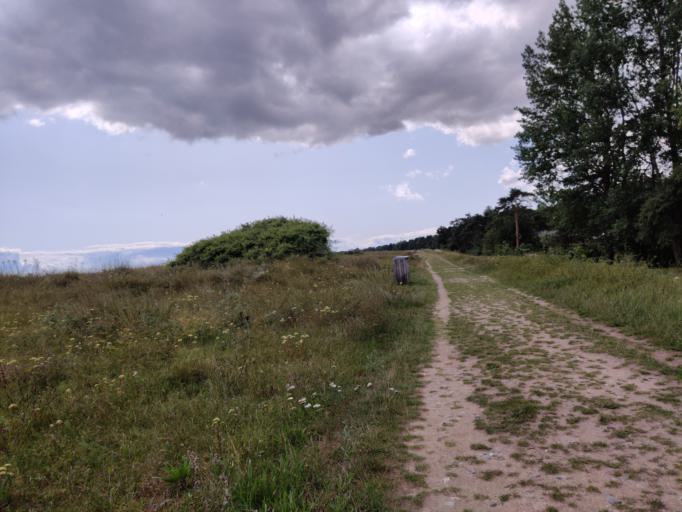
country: DK
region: Zealand
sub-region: Guldborgsund Kommune
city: Nykobing Falster
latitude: 54.7074
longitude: 11.9851
